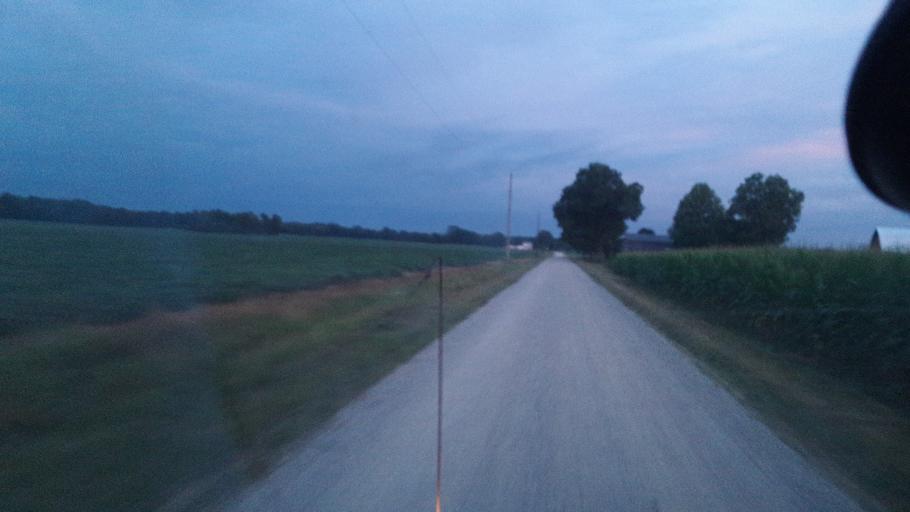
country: US
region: Ohio
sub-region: Defiance County
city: Hicksville
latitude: 41.3676
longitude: -84.8086
